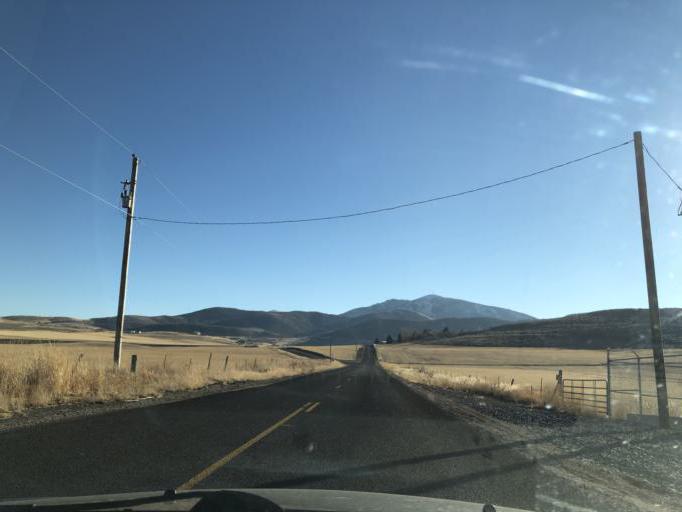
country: US
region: Utah
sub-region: Cache County
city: Wellsville
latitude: 41.6017
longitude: -111.9298
